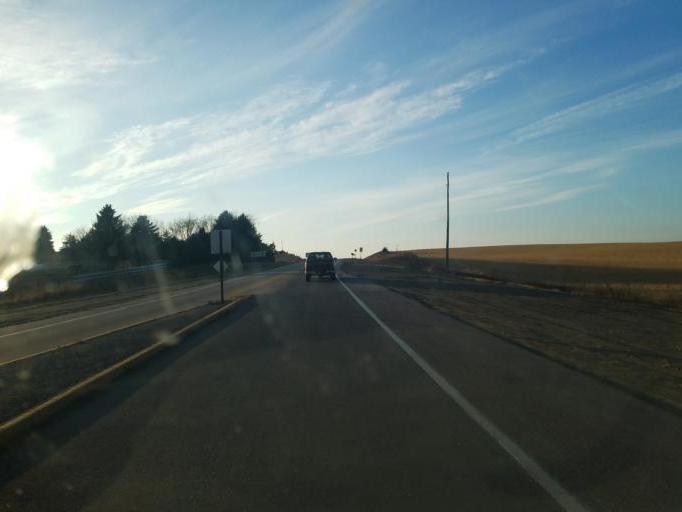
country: US
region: South Dakota
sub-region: Yankton County
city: Yankton
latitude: 42.7287
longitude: -97.4083
